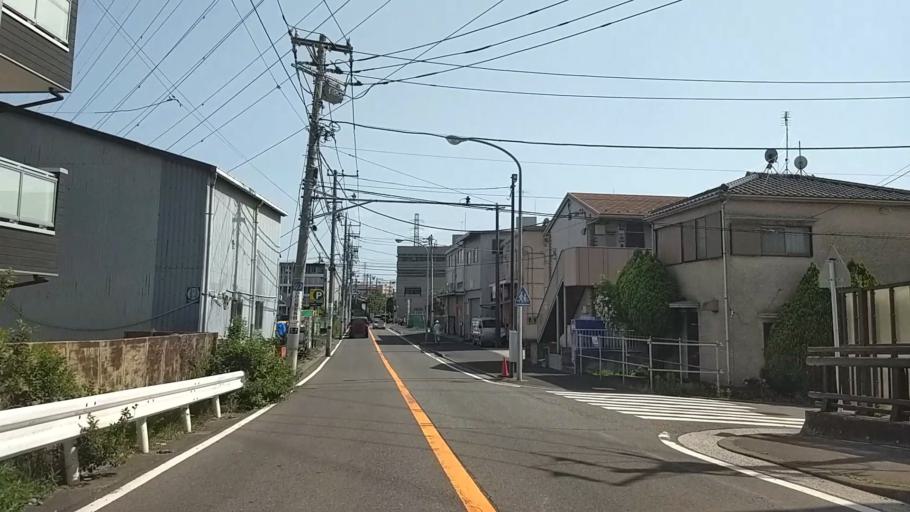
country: JP
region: Kanagawa
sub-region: Kawasaki-shi
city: Kawasaki
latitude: 35.5326
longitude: 139.6468
